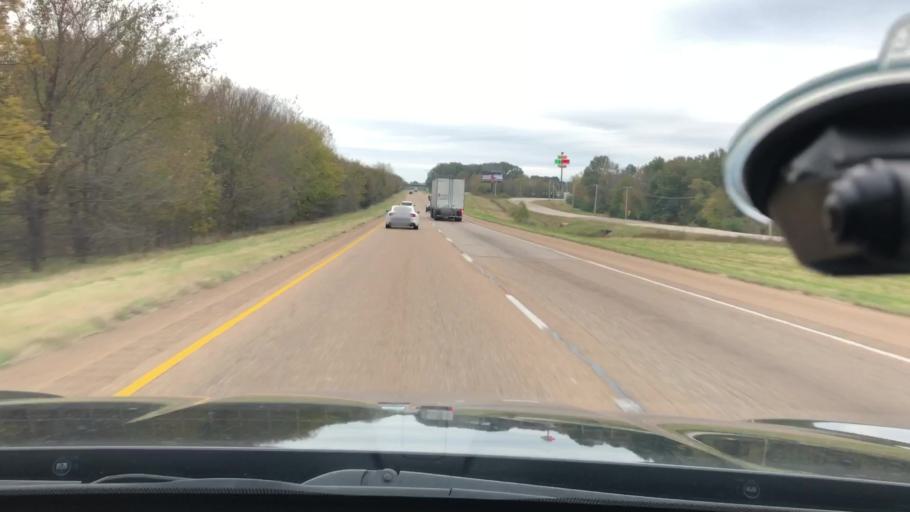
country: US
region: Arkansas
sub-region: Nevada County
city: Prescott
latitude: 33.8258
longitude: -93.4024
